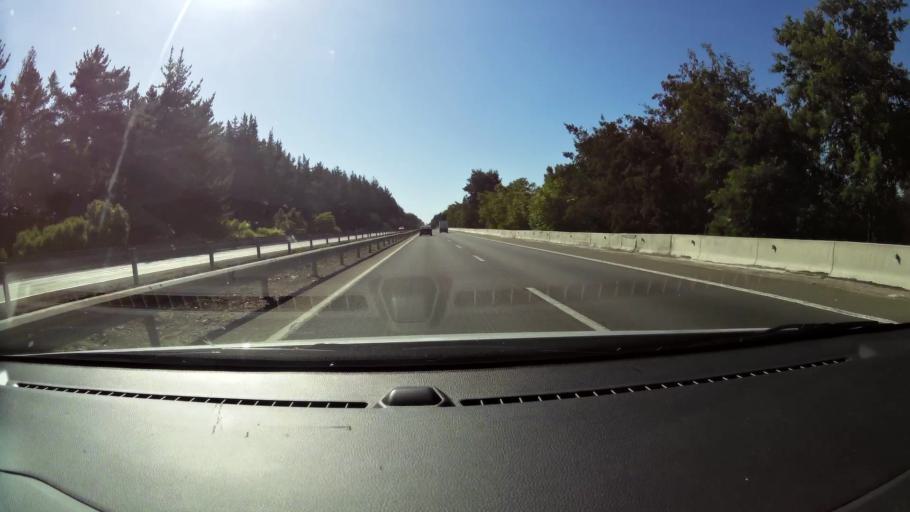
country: CL
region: Valparaiso
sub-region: Provincia de Marga Marga
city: Quilpue
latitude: -33.1709
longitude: -71.5231
